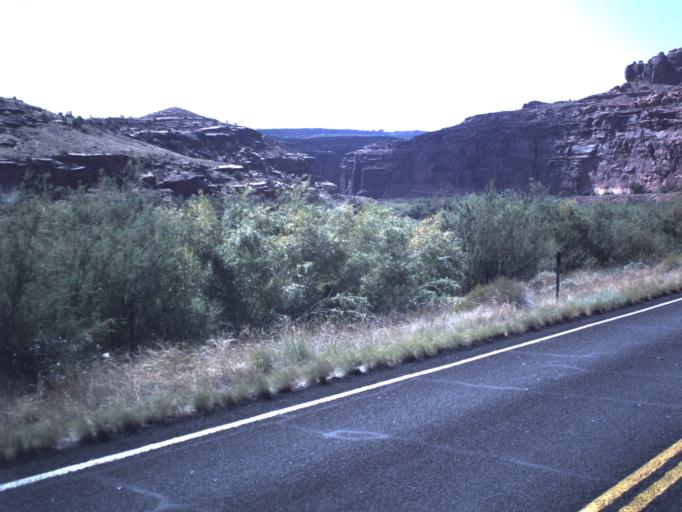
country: US
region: Utah
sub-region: Grand County
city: Moab
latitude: 38.5794
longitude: -109.6385
